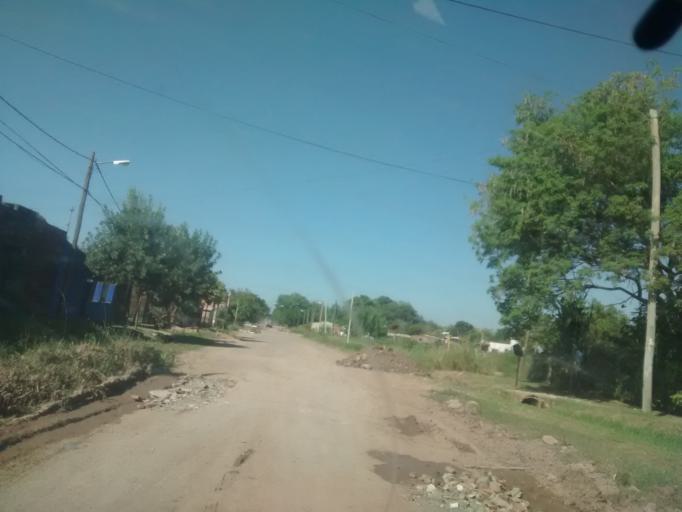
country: AR
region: Chaco
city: Resistencia
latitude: -27.4465
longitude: -58.9671
